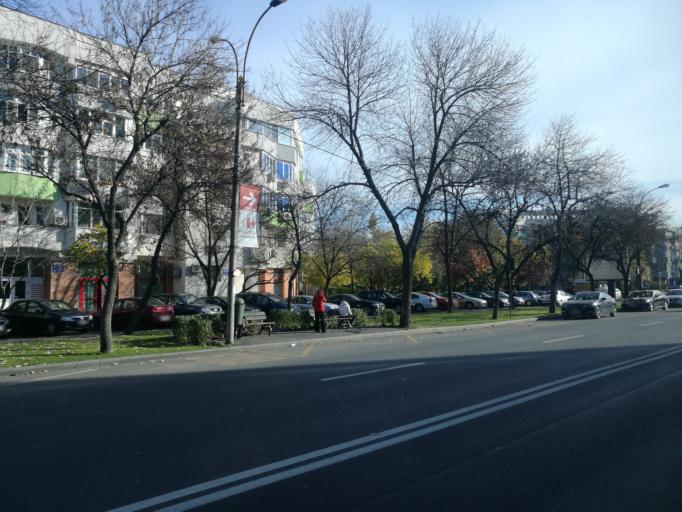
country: RO
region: Bucuresti
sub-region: Municipiul Bucuresti
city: Bucharest
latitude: 44.4846
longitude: 26.0922
